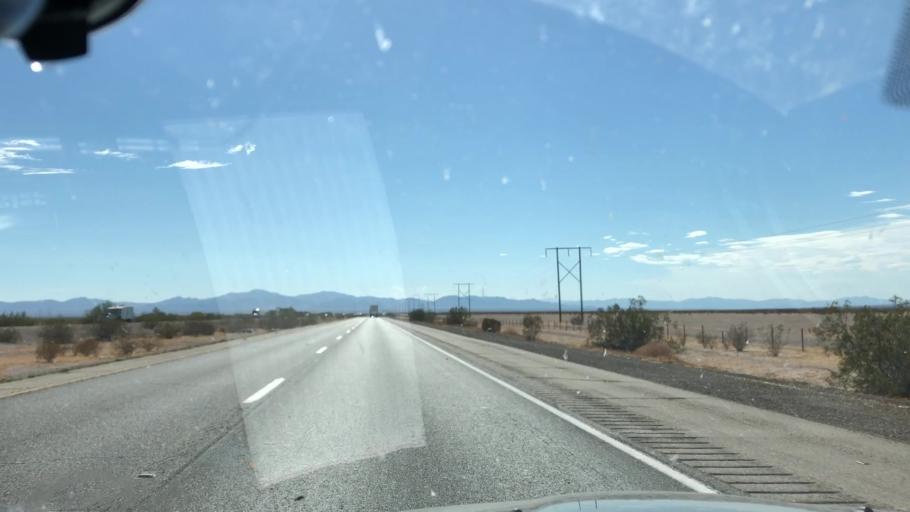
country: US
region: California
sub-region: Riverside County
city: Mesa Verde
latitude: 33.6062
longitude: -114.9342
